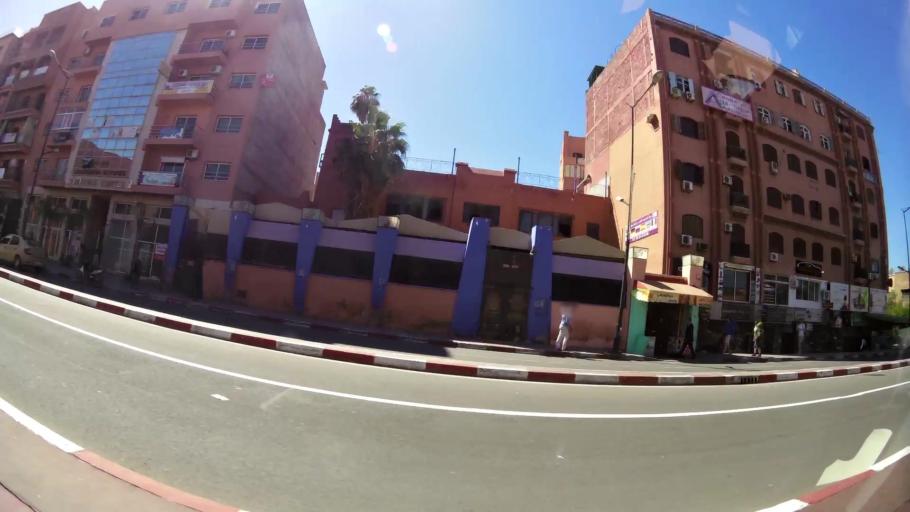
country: MA
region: Marrakech-Tensift-Al Haouz
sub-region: Marrakech
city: Marrakesh
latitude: 31.6331
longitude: -8.0050
